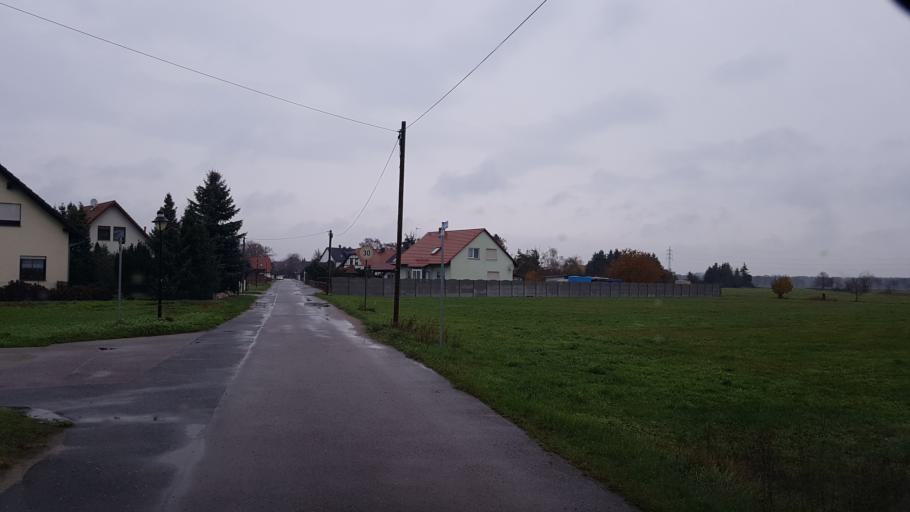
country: DE
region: Brandenburg
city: Herzberg
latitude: 51.6501
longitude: 13.2206
